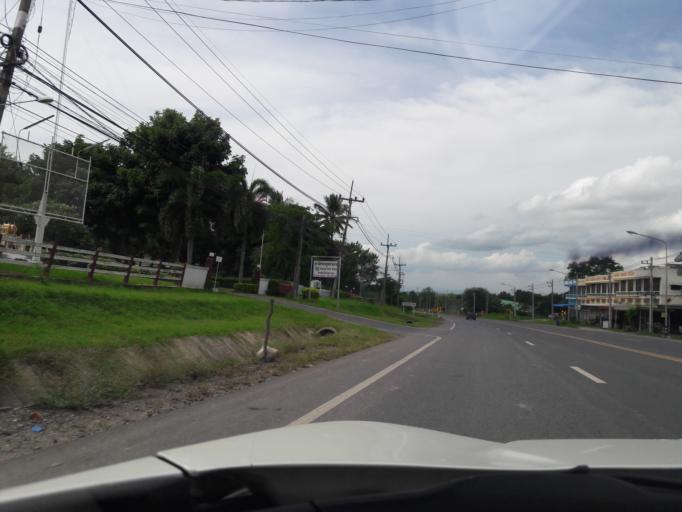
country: TH
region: Lop Buri
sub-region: Amphoe Tha Luang
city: Tha Luang
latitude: 15.0713
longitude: 101.1009
